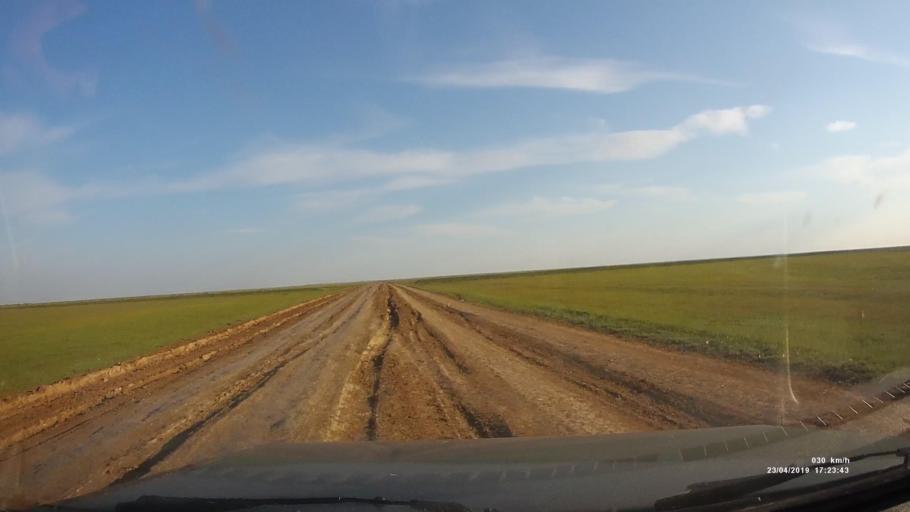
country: RU
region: Kalmykiya
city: Priyutnoye
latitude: 46.1605
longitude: 43.5080
